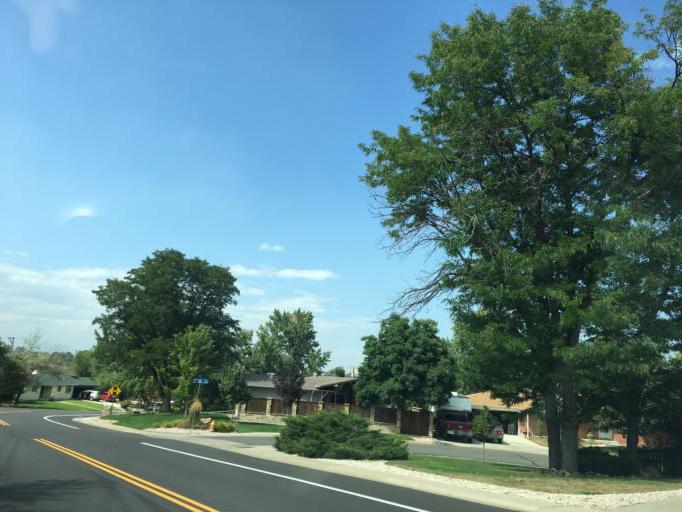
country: US
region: Colorado
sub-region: Jefferson County
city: Applewood
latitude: 39.7606
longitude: -105.1295
